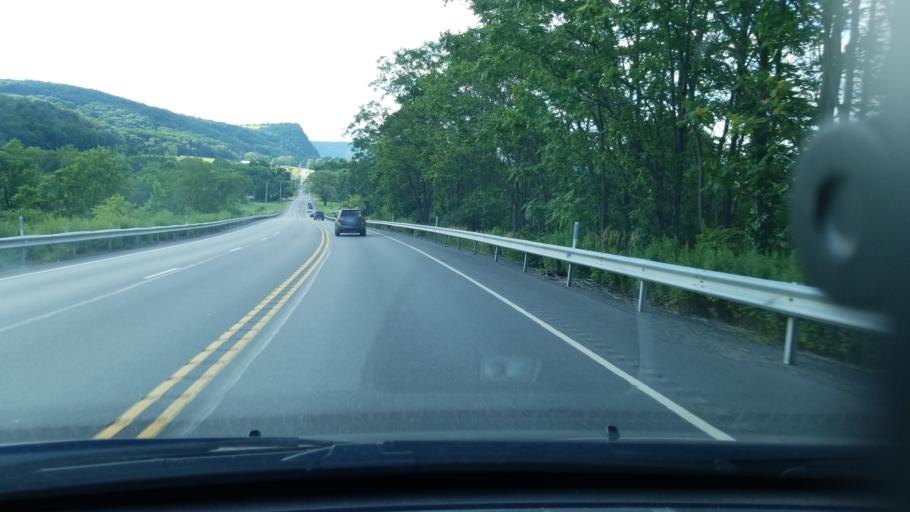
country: US
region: Pennsylvania
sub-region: Montour County
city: Mechanicsville
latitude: 40.9286
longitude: -76.5896
